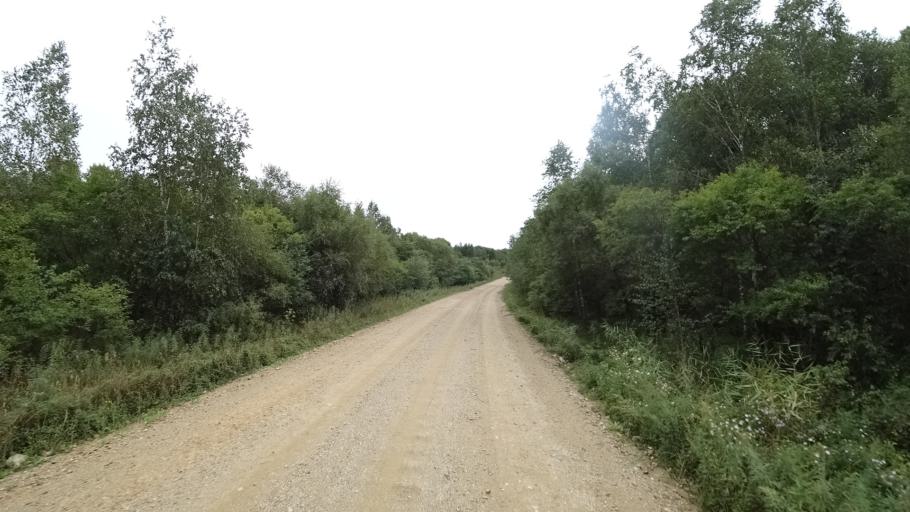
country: RU
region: Primorskiy
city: Lyalichi
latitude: 44.0659
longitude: 132.4782
